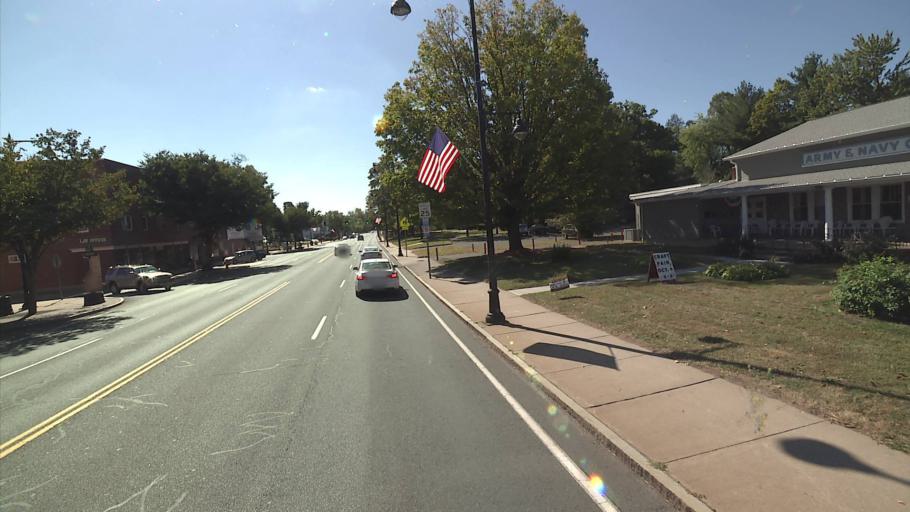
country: US
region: Connecticut
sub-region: Hartford County
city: Manchester
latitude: 41.7674
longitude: -72.5206
